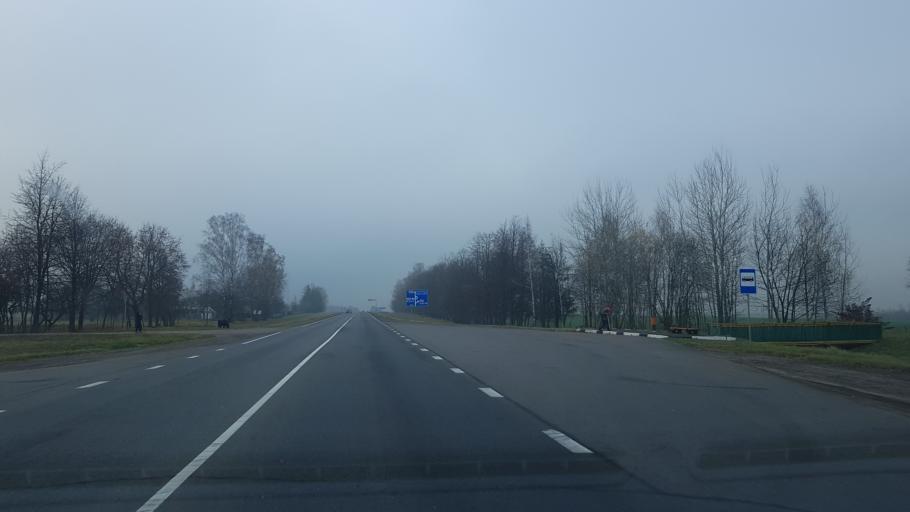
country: BY
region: Mogilev
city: Babruysk
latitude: 53.1781
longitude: 29.3467
